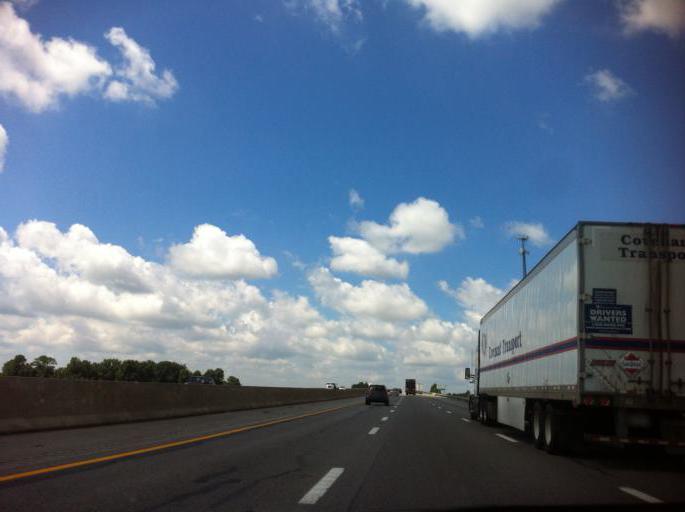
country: US
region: Ohio
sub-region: Huron County
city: Monroeville
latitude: 41.3356
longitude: -82.6906
